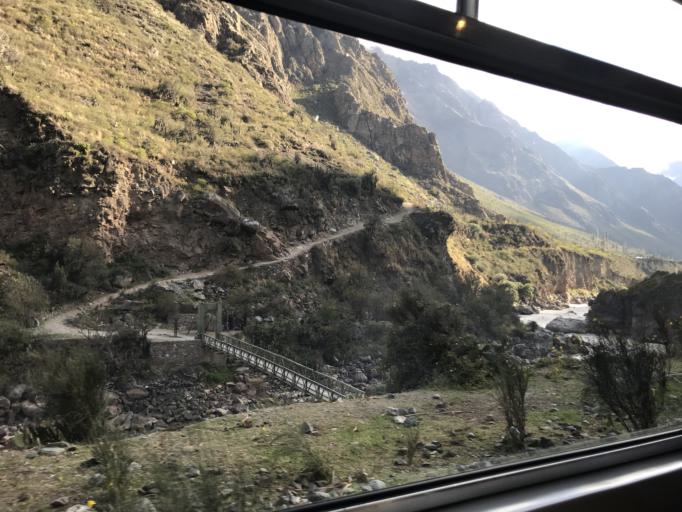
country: PE
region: Cusco
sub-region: Provincia de Urubamba
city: Ollantaytambo
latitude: -13.2155
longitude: -72.3840
